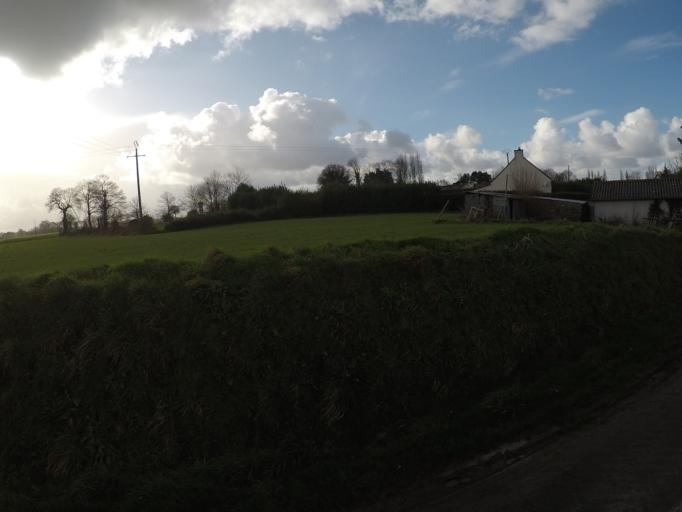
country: FR
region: Brittany
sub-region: Departement des Cotes-d'Armor
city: Goudelin
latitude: 48.6150
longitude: -3.0014
